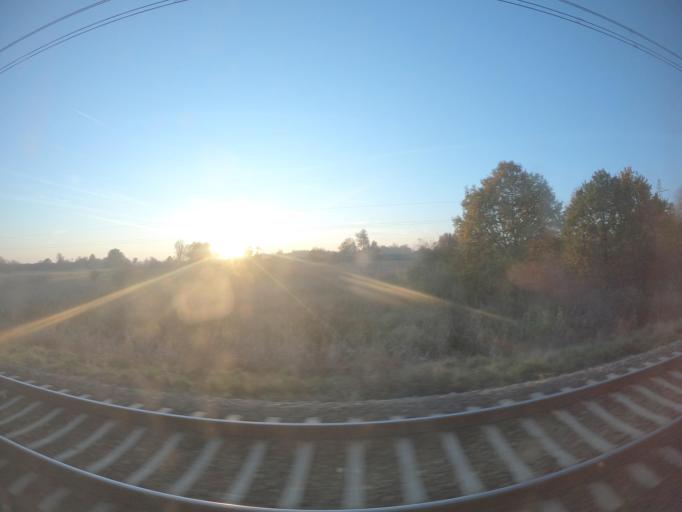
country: PL
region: Lubusz
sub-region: Powiat gorzowski
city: Kostrzyn nad Odra
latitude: 52.5696
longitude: 14.6452
